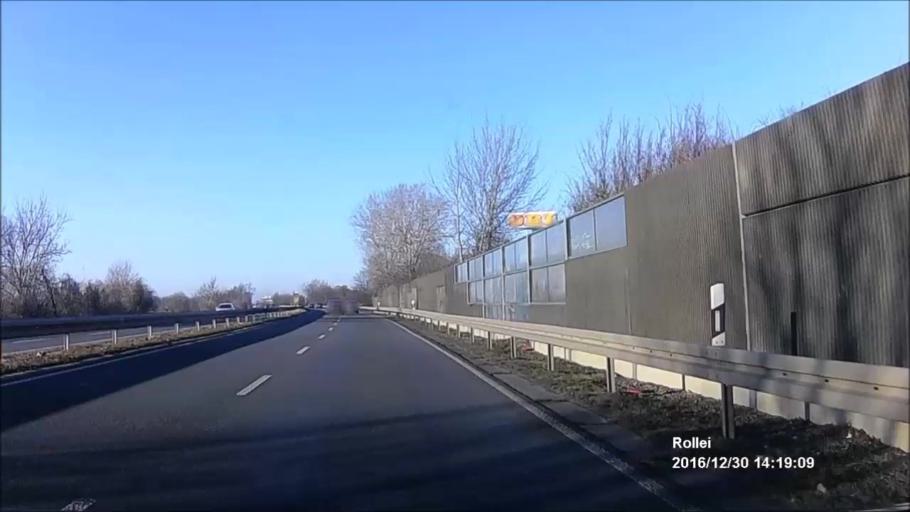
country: DE
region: Thuringia
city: Erfurt
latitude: 50.9994
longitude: 10.9996
